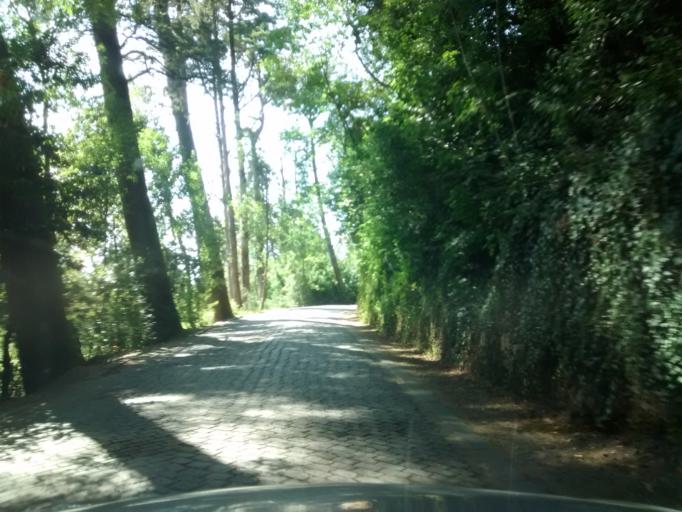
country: PT
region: Aveiro
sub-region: Mealhada
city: Pampilhosa do Botao
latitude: 40.3784
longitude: -8.3679
